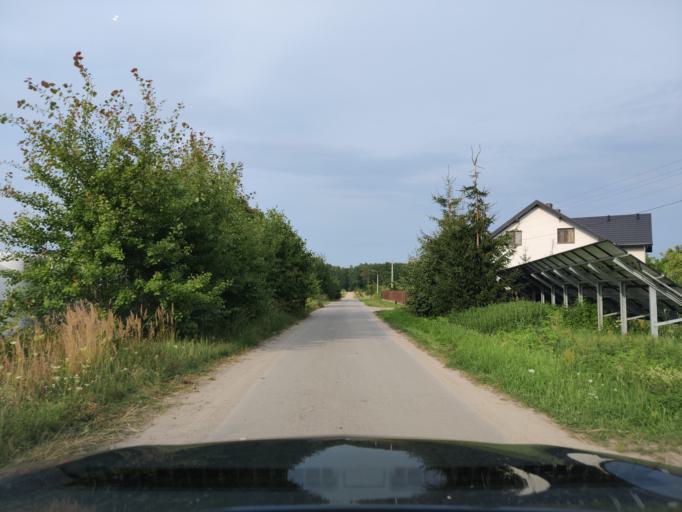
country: PL
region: Masovian Voivodeship
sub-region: Powiat pultuski
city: Obryte
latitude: 52.6970
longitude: 21.2044
